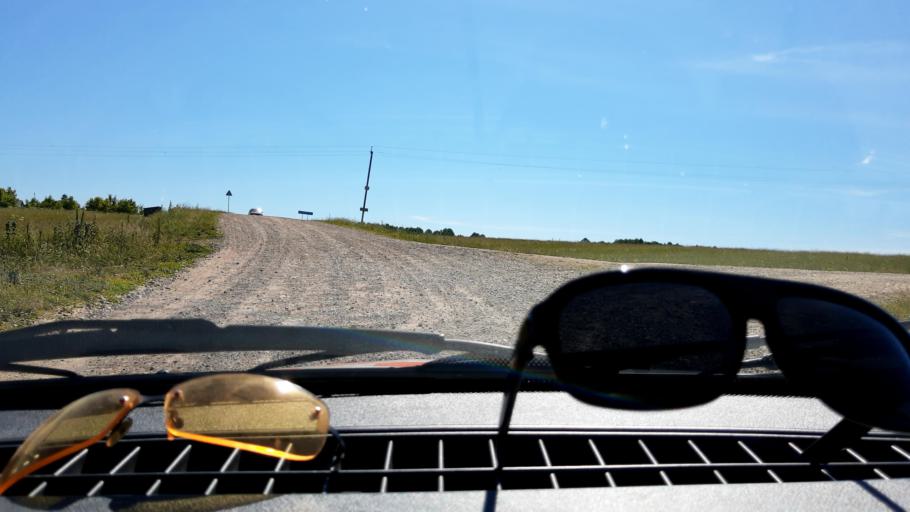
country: RU
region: Bashkortostan
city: Ulu-Telyak
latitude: 54.7968
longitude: 57.0105
